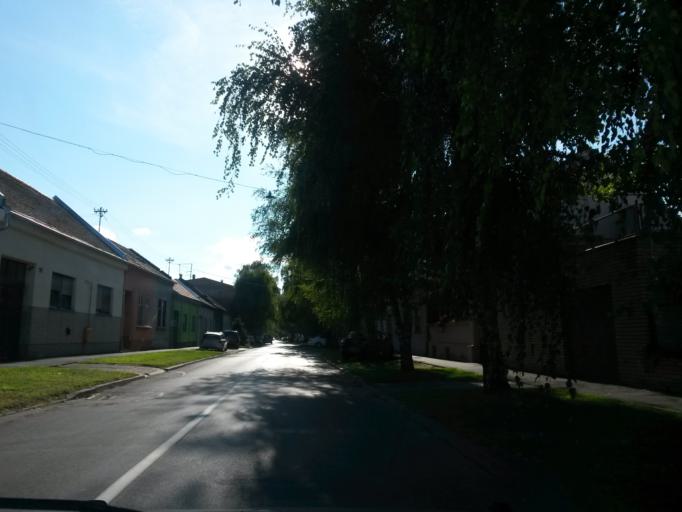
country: HR
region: Osjecko-Baranjska
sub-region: Grad Osijek
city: Osijek
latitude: 45.5526
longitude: 18.7120
